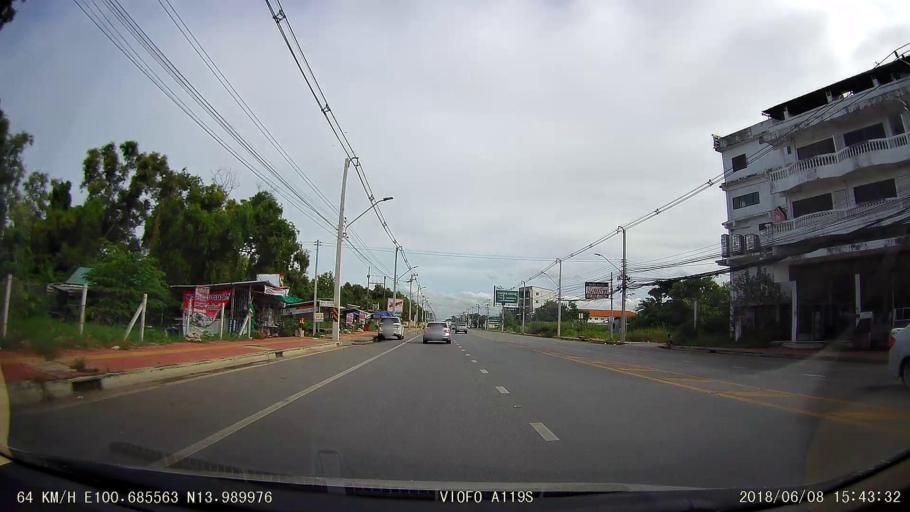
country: TH
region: Pathum Thani
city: Thanyaburi
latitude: 13.9898
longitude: 100.6856
